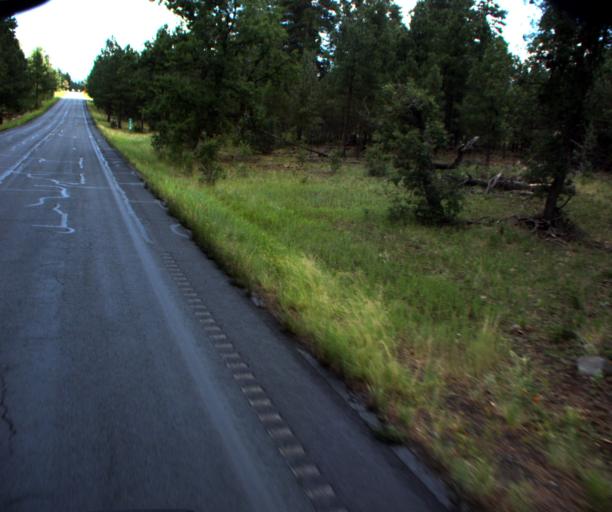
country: US
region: Arizona
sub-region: Gila County
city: Pine
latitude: 34.5042
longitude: -111.4688
